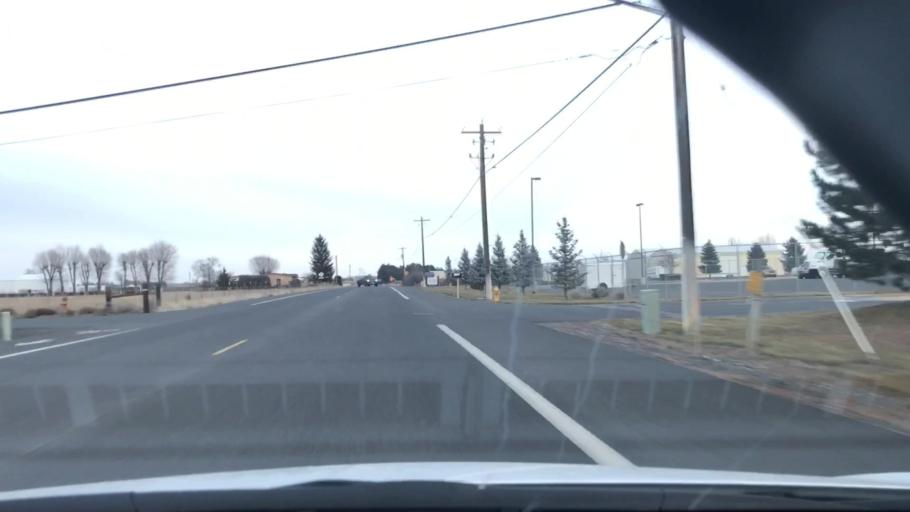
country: US
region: Washington
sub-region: Grant County
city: Moses Lake
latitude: 47.1455
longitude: -119.2418
